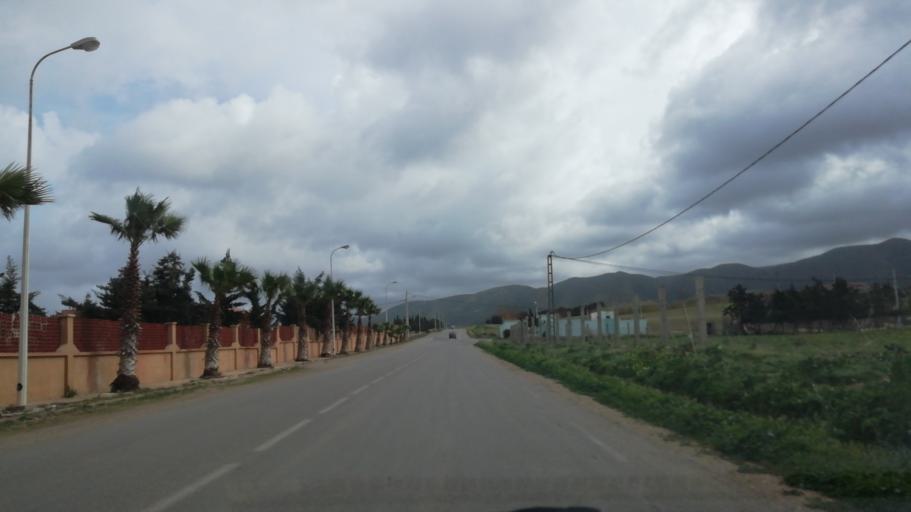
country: DZ
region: Oran
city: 'Ain el Turk
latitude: 35.7004
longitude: -0.8854
